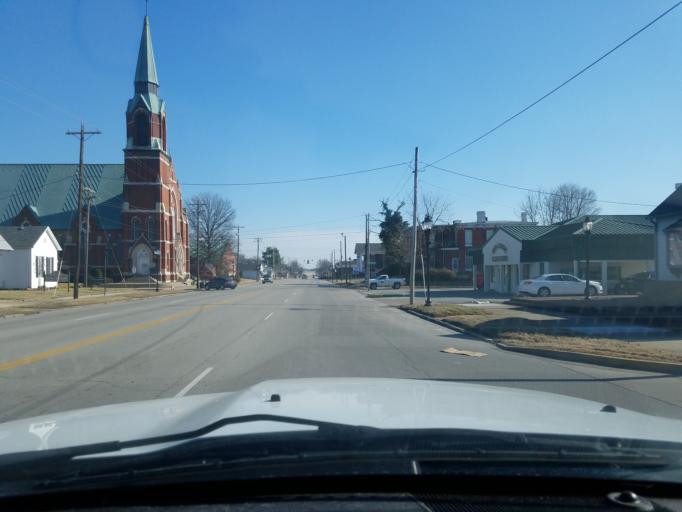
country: US
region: Kentucky
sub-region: Henderson County
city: Henderson
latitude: 37.8391
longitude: -87.5876
